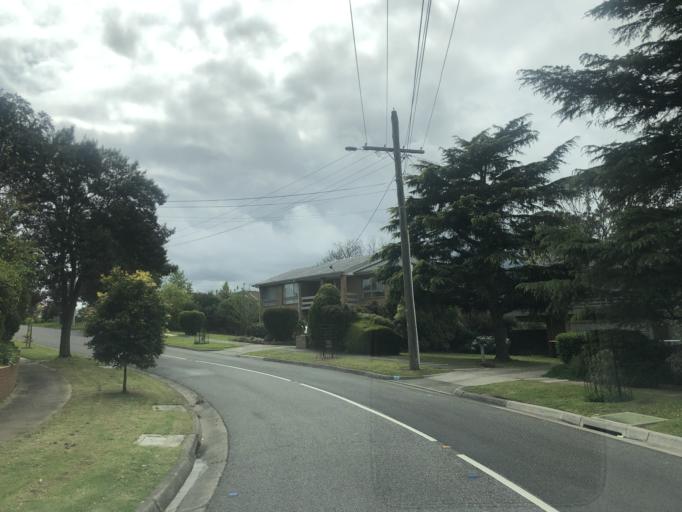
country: AU
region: Victoria
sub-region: Greater Dandenong
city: Dandenong North
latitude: -37.9546
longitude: 145.2249
